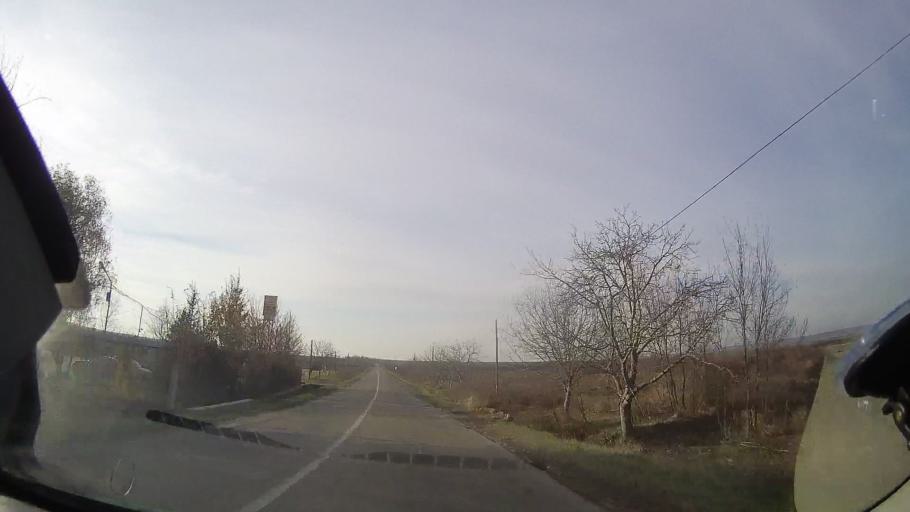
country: RO
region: Bihor
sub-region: Comuna Ciuhoiu
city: Ciuhoiu
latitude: 47.2269
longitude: 22.1516
